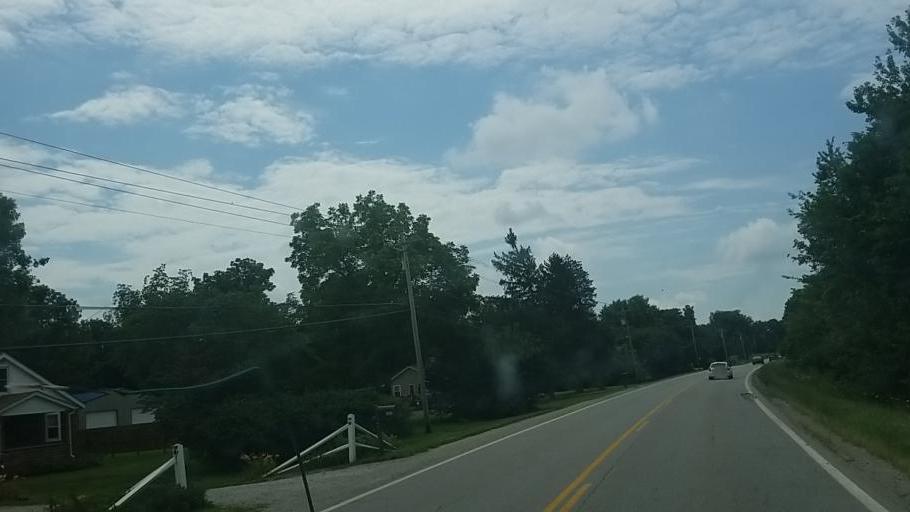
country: US
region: Ohio
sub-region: Franklin County
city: Obetz
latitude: 39.8305
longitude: -82.9757
